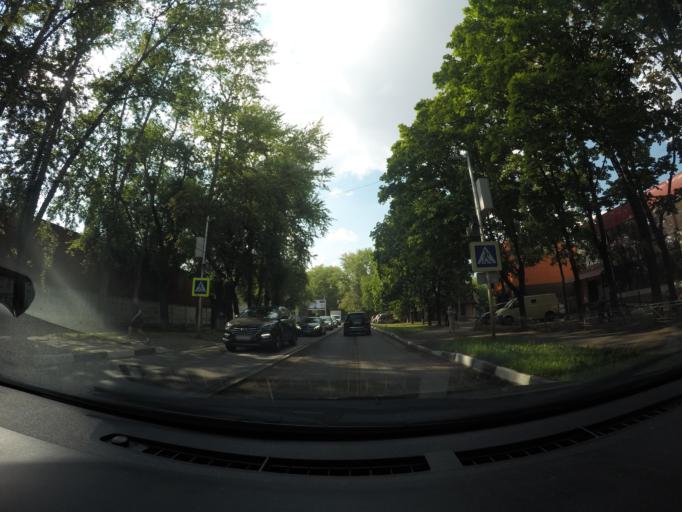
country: RU
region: Moskovskaya
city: Tomilino
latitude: 55.6652
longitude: 37.9281
